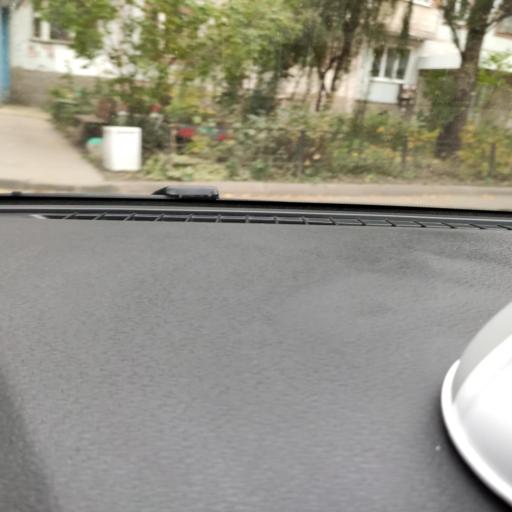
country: RU
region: Samara
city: Samara
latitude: 53.1986
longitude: 50.1487
